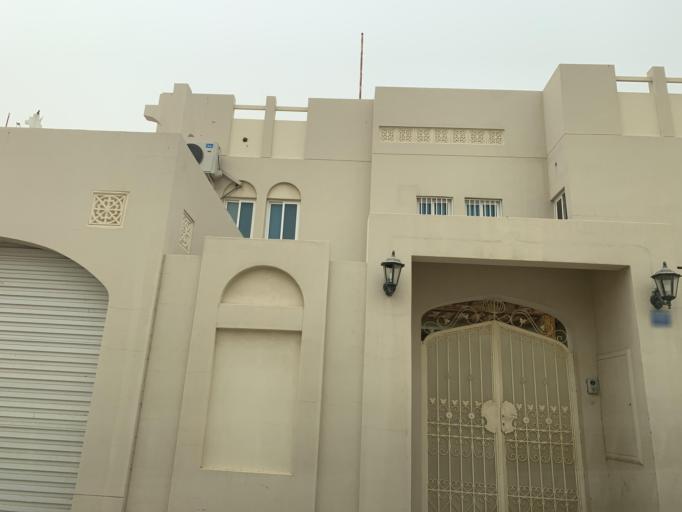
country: BH
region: Central Governorate
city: Madinat Hamad
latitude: 26.1359
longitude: 50.5140
